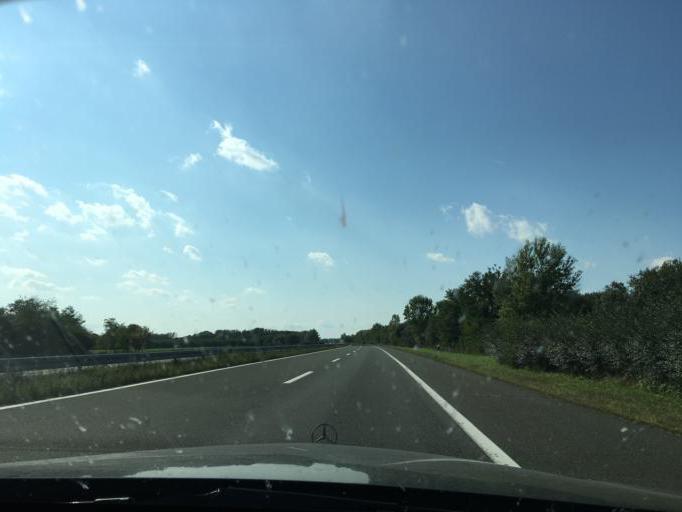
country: HR
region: Medimurska
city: Hodosan
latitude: 46.4135
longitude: 16.6220
